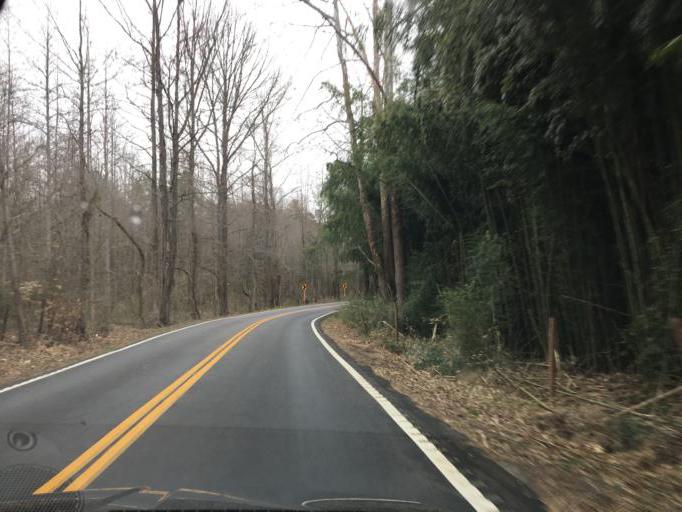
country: US
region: South Carolina
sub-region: Greenville County
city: Travelers Rest
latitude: 34.9379
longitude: -82.5177
